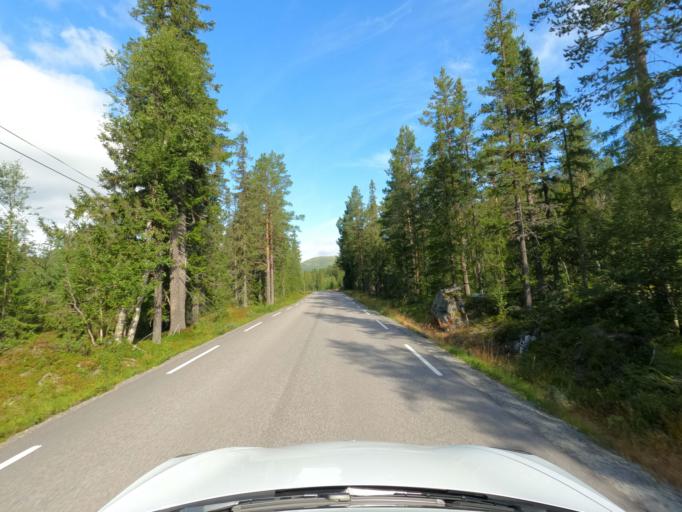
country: NO
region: Telemark
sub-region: Tinn
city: Rjukan
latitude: 60.1112
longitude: 8.7259
